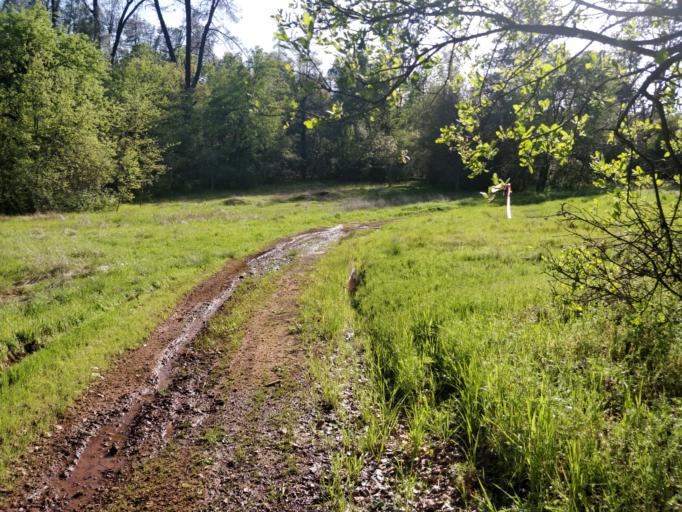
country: US
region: California
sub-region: Shasta County
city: Shasta Lake
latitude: 40.6685
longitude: -122.3683
